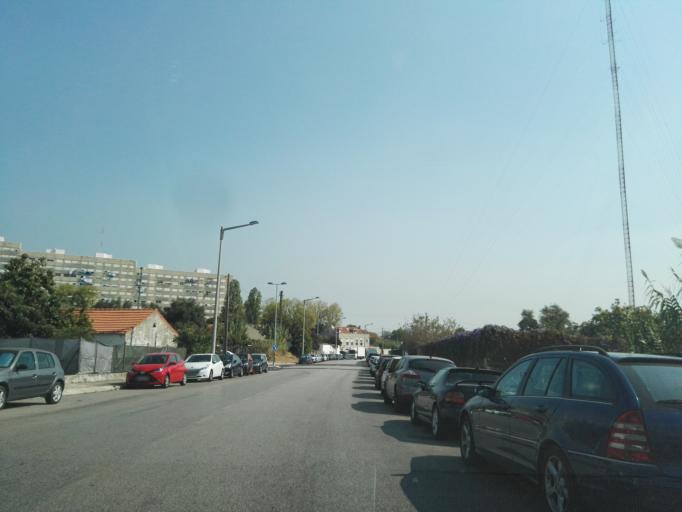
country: PT
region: Lisbon
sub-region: Loures
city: Moscavide
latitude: 38.7538
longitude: -9.1073
